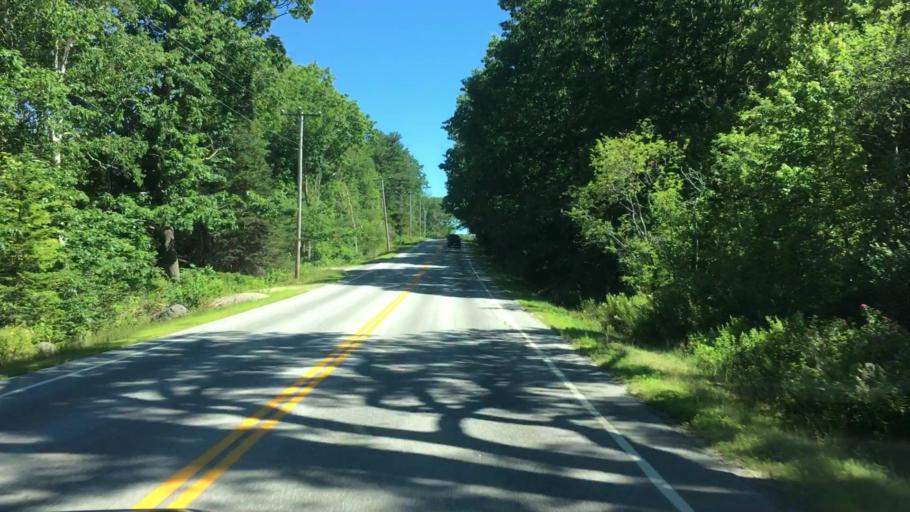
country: US
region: Maine
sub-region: Hancock County
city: Sedgwick
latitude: 44.3548
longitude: -68.6675
